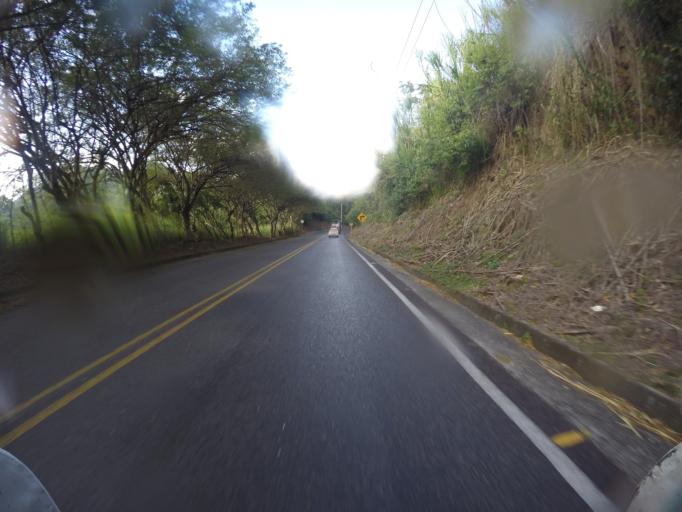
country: CO
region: Valle del Cauca
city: Cartago
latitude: 4.7293
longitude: -75.8697
